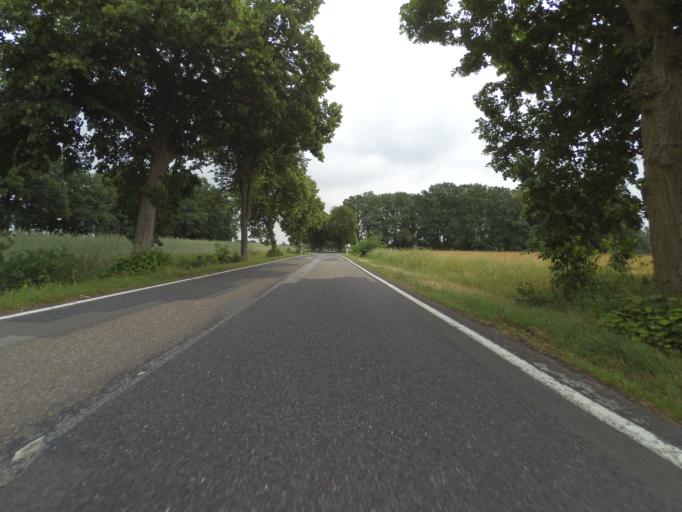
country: DE
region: Mecklenburg-Vorpommern
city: Siggelkow
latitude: 53.3631
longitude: 12.0114
